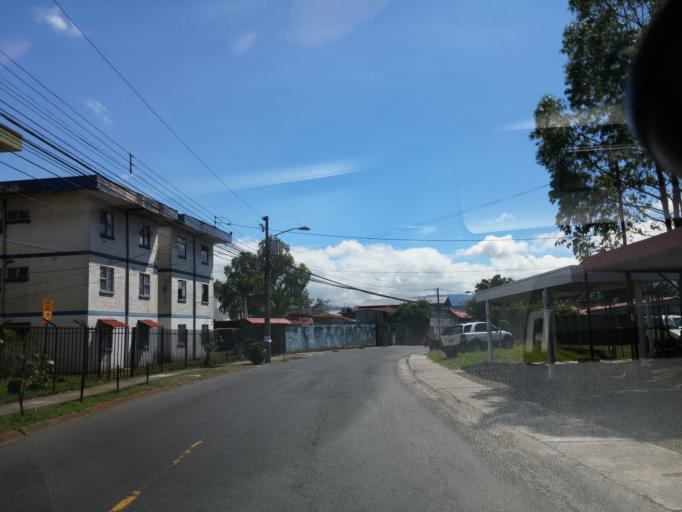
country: CR
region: San Jose
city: San Jose
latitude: 9.9221
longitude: -84.0869
